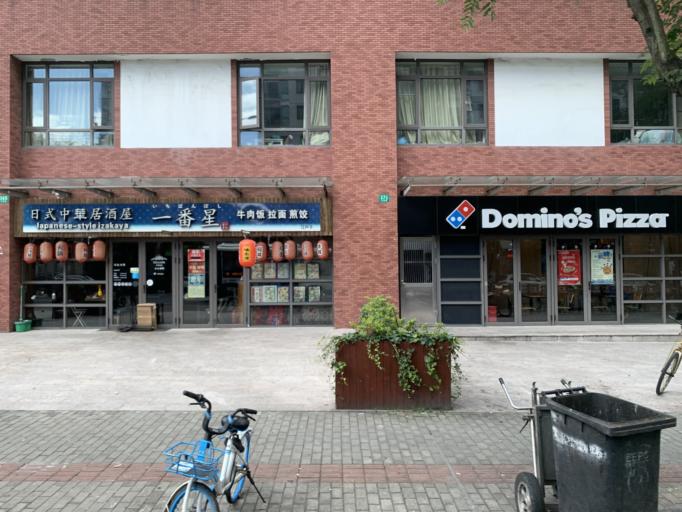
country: CN
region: Shanghai Shi
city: Huamu
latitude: 31.2026
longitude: 121.5302
